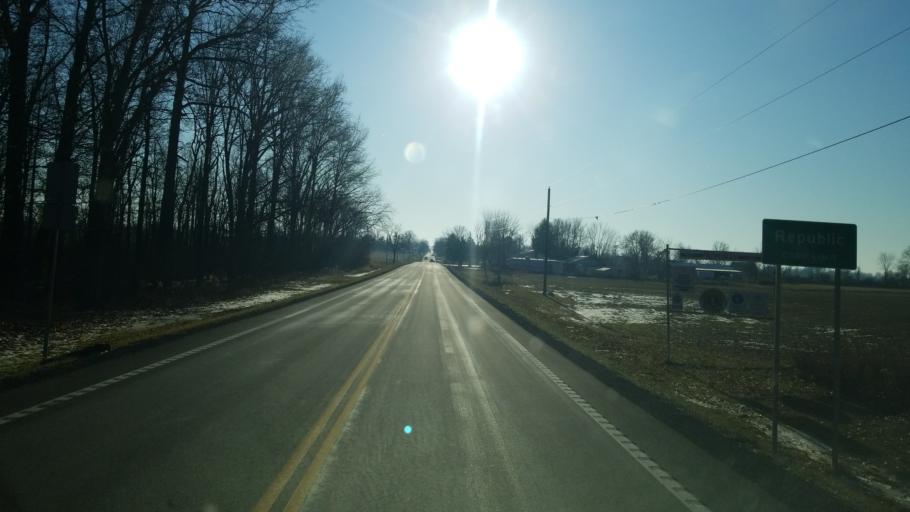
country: US
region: Ohio
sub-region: Sandusky County
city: Green Springs
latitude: 41.1326
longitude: -83.0100
